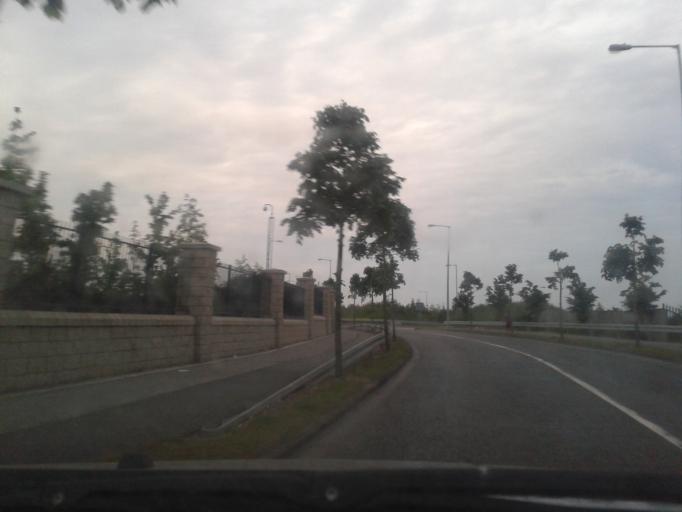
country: IE
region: Leinster
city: Kinsealy-Drinan
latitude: 53.4473
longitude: -6.2070
